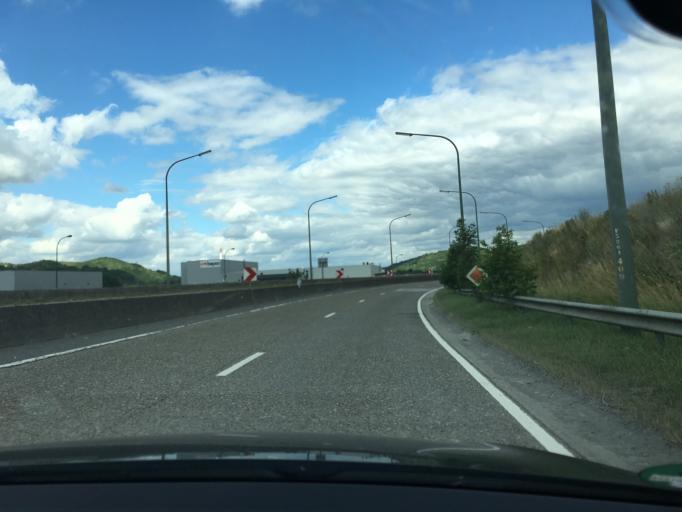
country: BE
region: Wallonia
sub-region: Province de Liege
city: Engis
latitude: 50.5618
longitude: 5.3643
